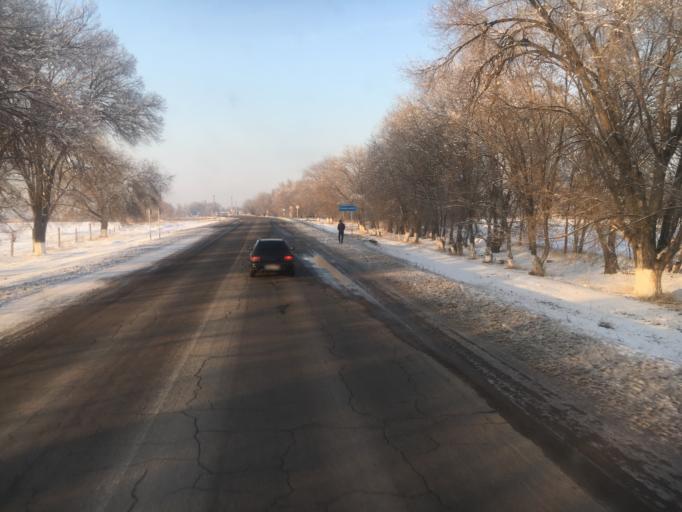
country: KZ
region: Almaty Oblysy
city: Burunday
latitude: 43.3293
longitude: 76.6622
